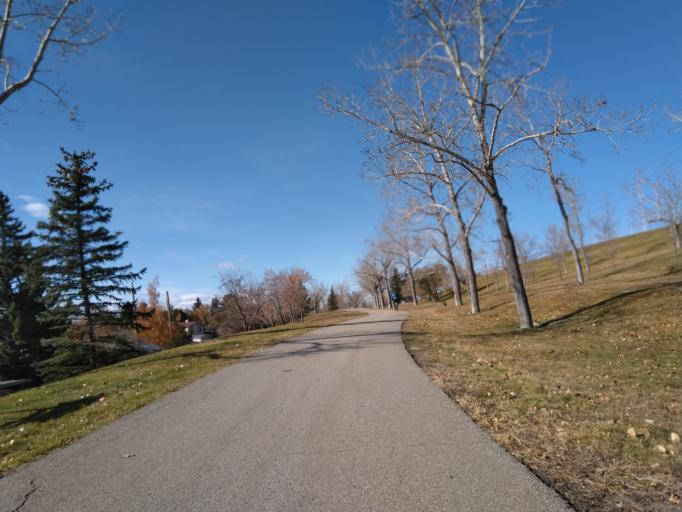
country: CA
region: Alberta
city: Calgary
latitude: 51.0930
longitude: -114.1112
